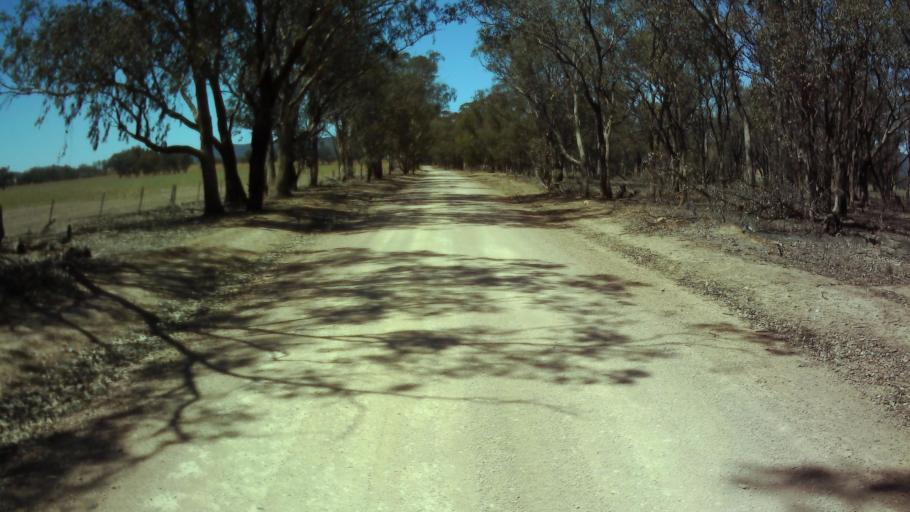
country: AU
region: New South Wales
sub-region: Weddin
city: Grenfell
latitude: -33.9237
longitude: 148.0784
